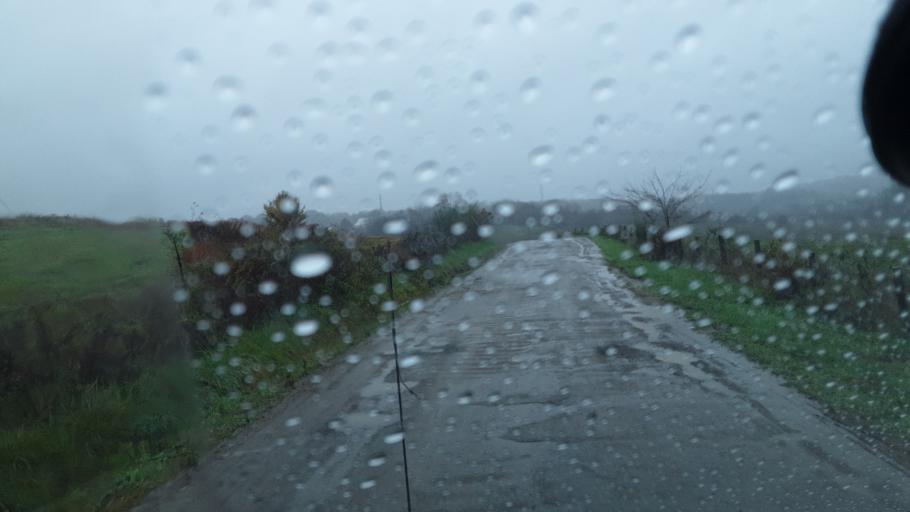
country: US
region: Ohio
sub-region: Vinton County
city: McArthur
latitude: 39.2253
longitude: -82.4682
